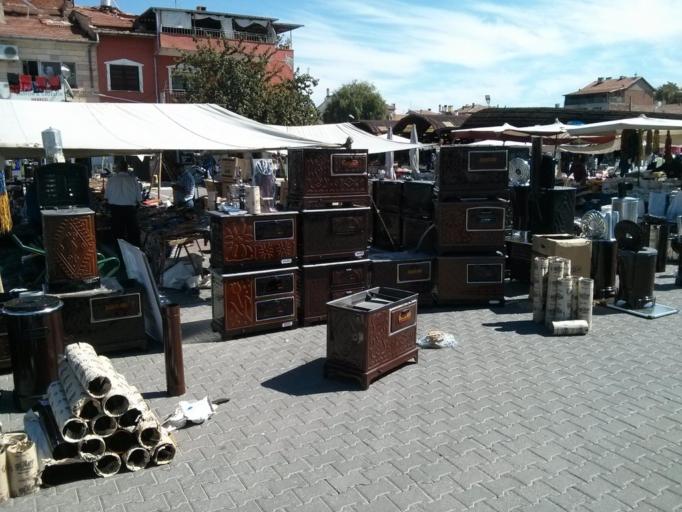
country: TR
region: Nevsehir
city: Avanos
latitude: 38.7148
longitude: 34.8443
